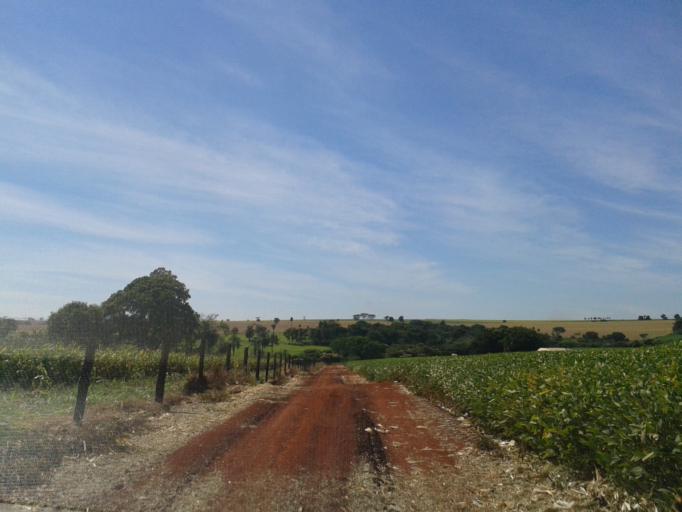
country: BR
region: Minas Gerais
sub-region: Capinopolis
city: Capinopolis
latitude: -18.6518
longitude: -49.7130
